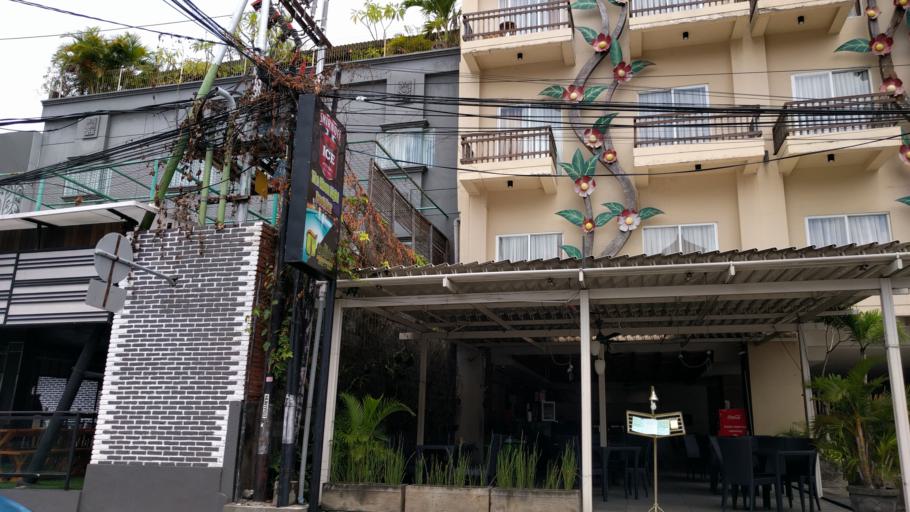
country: ID
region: Bali
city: Jabajero
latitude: -8.7366
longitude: 115.1672
